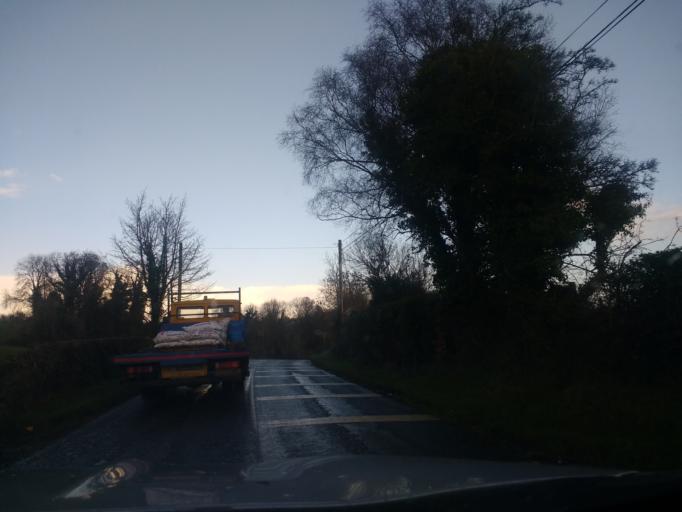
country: IE
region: Ulster
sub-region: County Donegal
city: Ramelton
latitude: 55.0557
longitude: -7.6365
